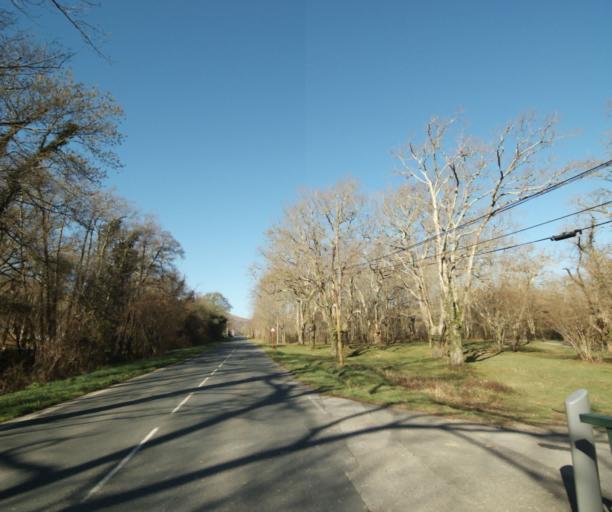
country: FR
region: Aquitaine
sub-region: Departement des Pyrenees-Atlantiques
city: Urrugne
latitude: 43.3342
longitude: -1.6808
